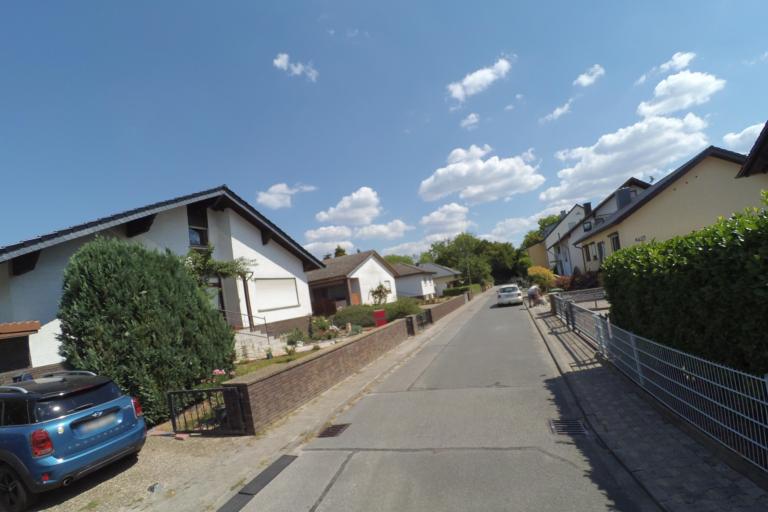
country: DE
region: Hesse
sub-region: Regierungsbezirk Darmstadt
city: Alsbach-Hahnlein
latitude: 49.7393
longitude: 8.5655
